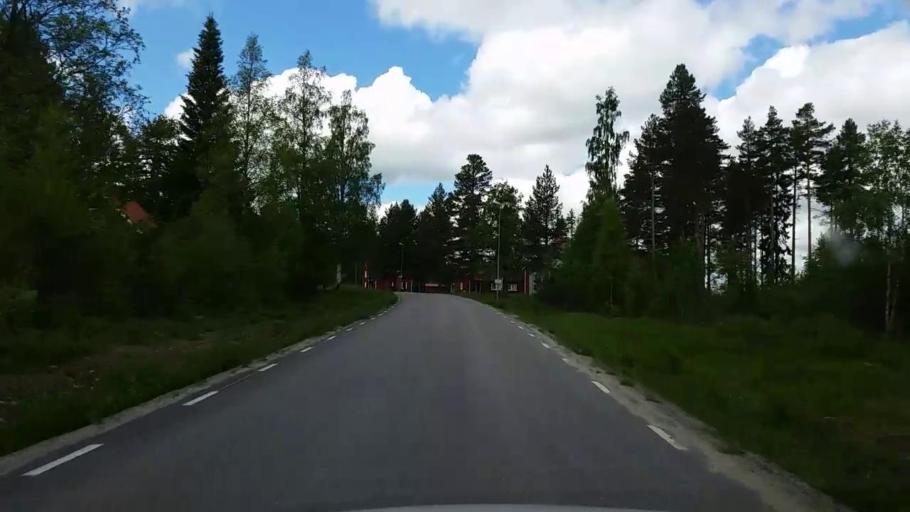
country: SE
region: Gaevleborg
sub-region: Bollnas Kommun
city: Vittsjo
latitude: 61.0979
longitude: 16.1642
